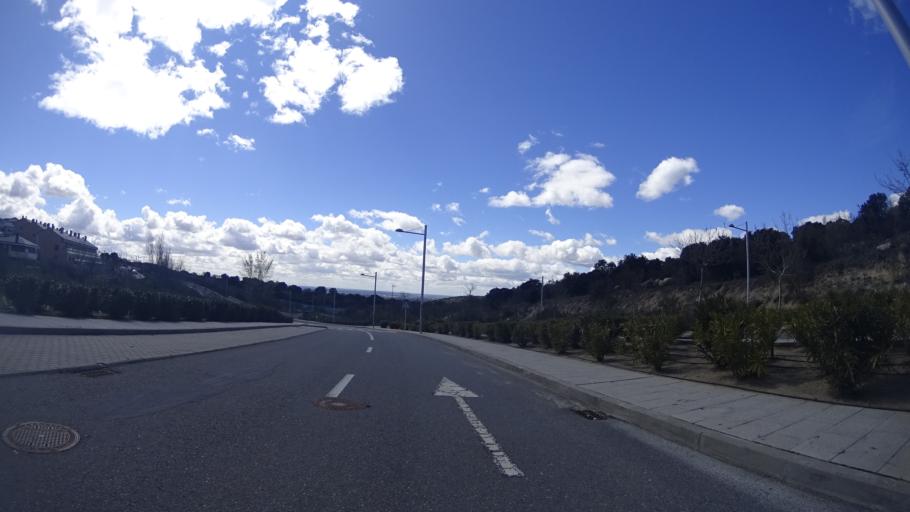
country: ES
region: Madrid
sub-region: Provincia de Madrid
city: Torrelodones
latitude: 40.5667
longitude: -3.9246
